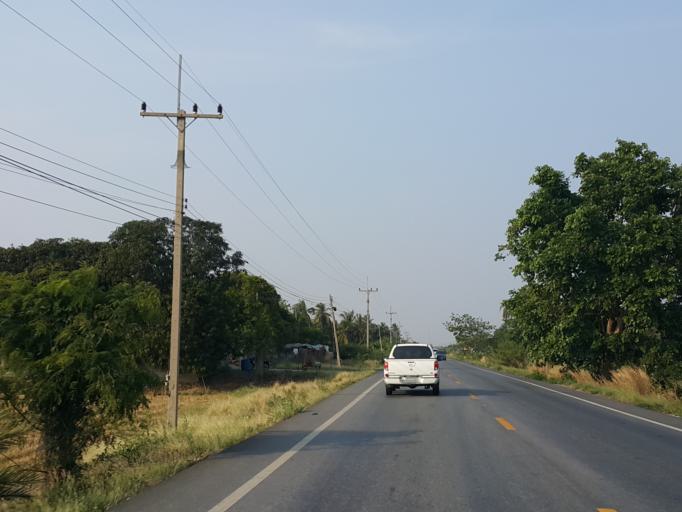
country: TH
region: Chai Nat
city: Hankha
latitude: 14.9754
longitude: 100.1014
